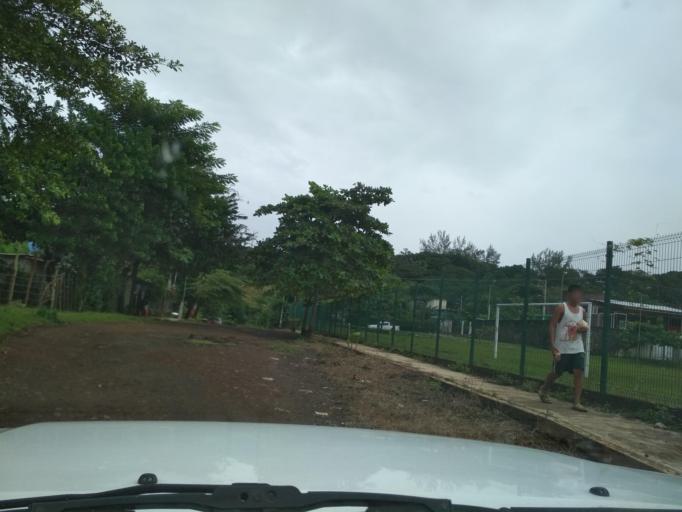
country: MX
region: Veracruz
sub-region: San Andres Tuxtla
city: Los Pinos
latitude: 18.4488
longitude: -95.2348
